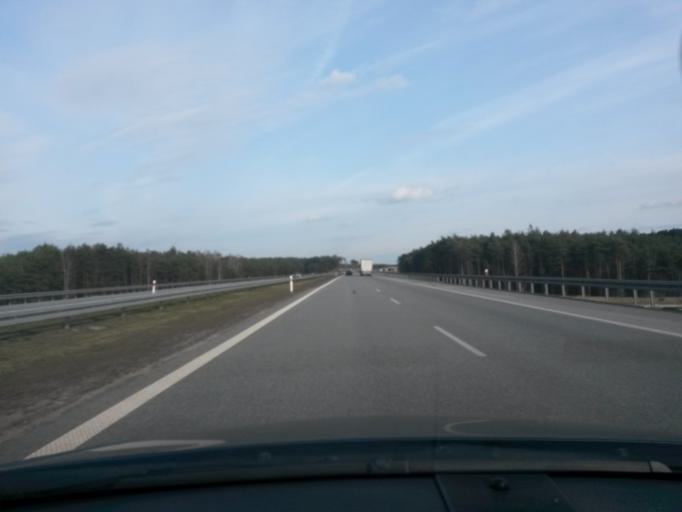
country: PL
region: Greater Poland Voivodeship
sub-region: Powiat turecki
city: Tuliszkow
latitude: 52.1477
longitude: 18.3041
